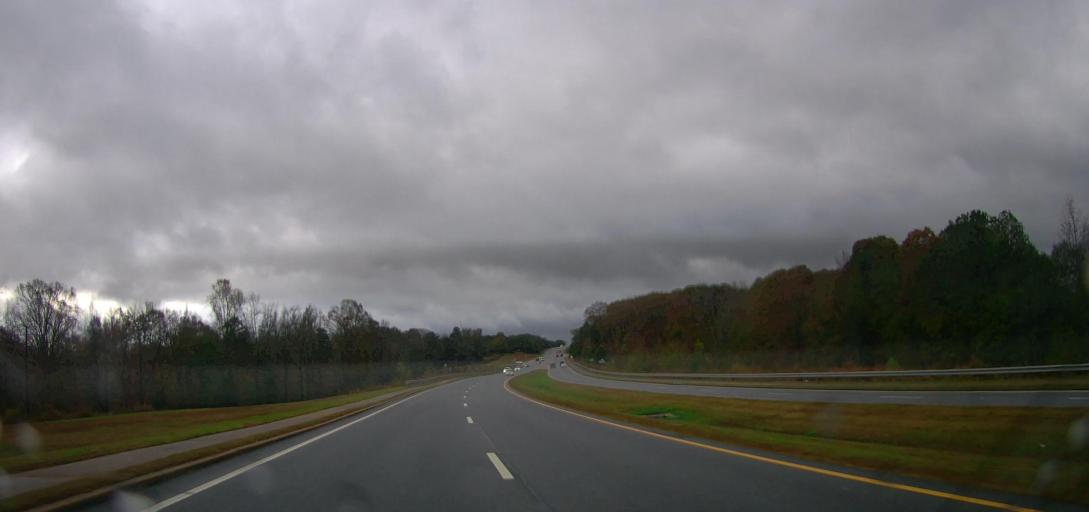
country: US
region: Georgia
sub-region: Jackson County
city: Nicholson
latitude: 34.1297
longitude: -83.4280
